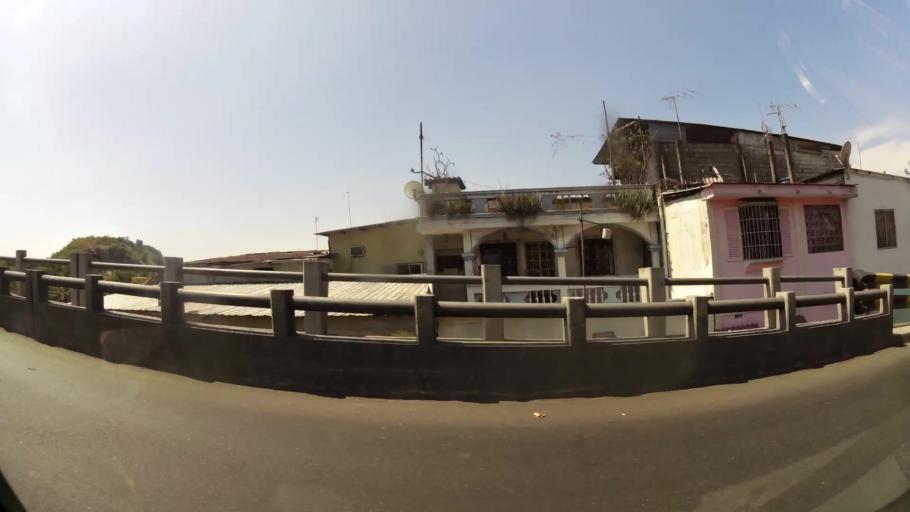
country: EC
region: Guayas
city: Guayaquil
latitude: -2.1904
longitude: -79.9123
